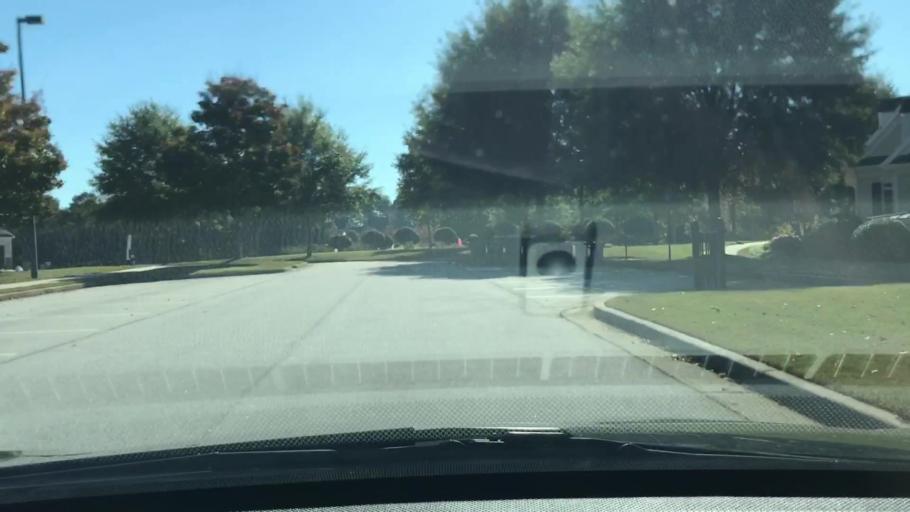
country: US
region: Georgia
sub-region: Carroll County
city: Villa Rica
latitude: 33.7981
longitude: -84.9169
